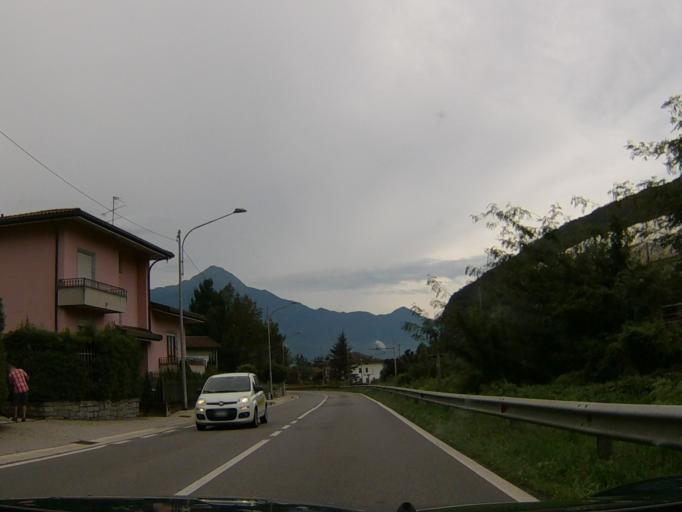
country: IT
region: Lombardy
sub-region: Provincia di Sondrio
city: Novate Mezzola
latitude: 46.2229
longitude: 9.4467
